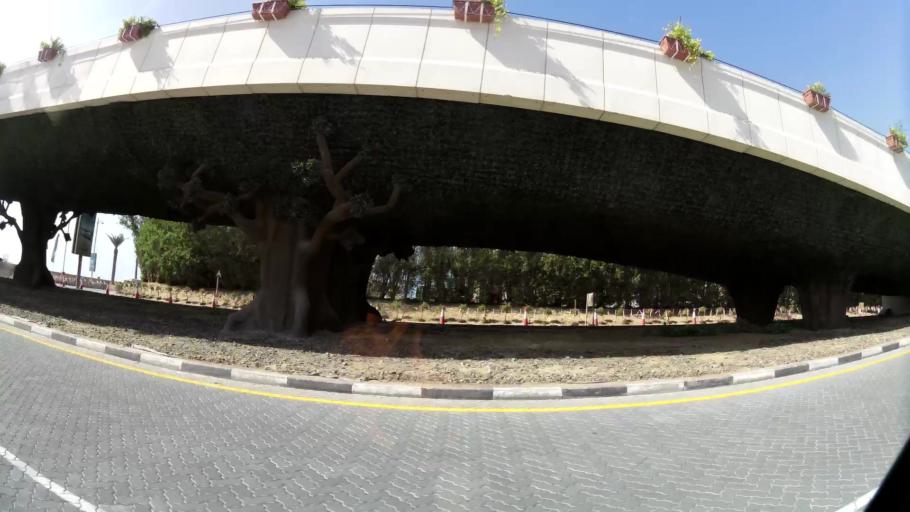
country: AE
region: Dubai
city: Dubai
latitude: 25.1256
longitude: 55.1126
